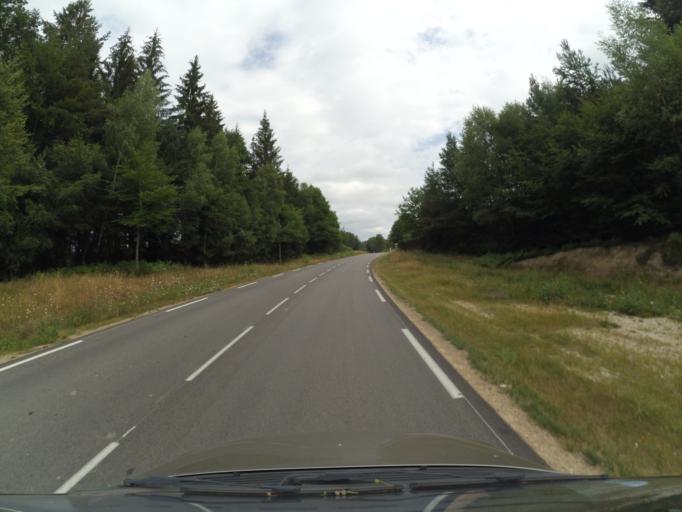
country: FR
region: Limousin
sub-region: Departement de la Correze
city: Ussel
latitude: 45.5848
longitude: 2.2903
